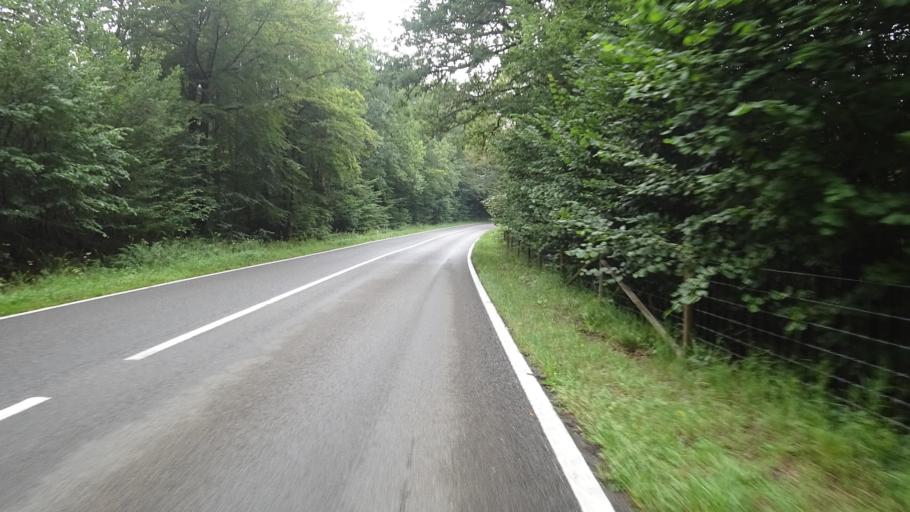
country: BE
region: Wallonia
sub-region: Province du Luxembourg
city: Chiny
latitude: 49.7844
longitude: 5.3321
